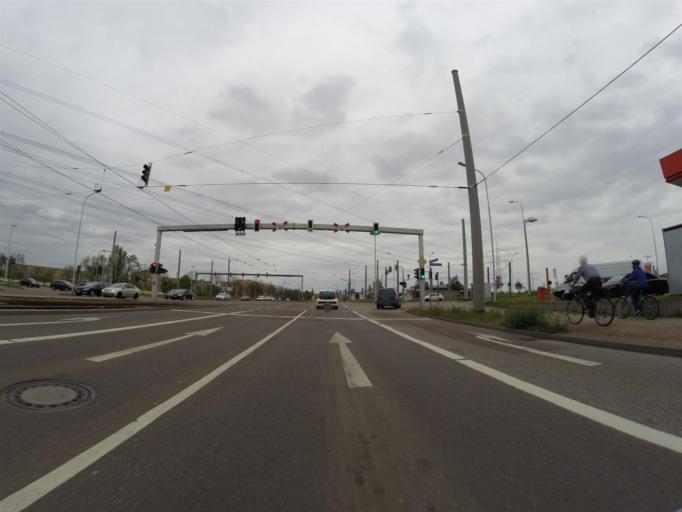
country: DE
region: Saxony-Anhalt
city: Schkopau
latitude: 51.4388
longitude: 11.9841
